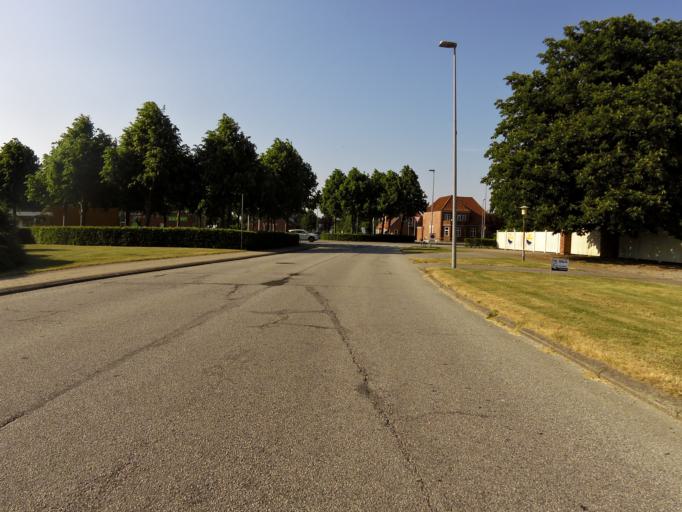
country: DK
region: South Denmark
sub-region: Haderslev Kommune
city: Vojens
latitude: 55.2440
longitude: 9.2930
